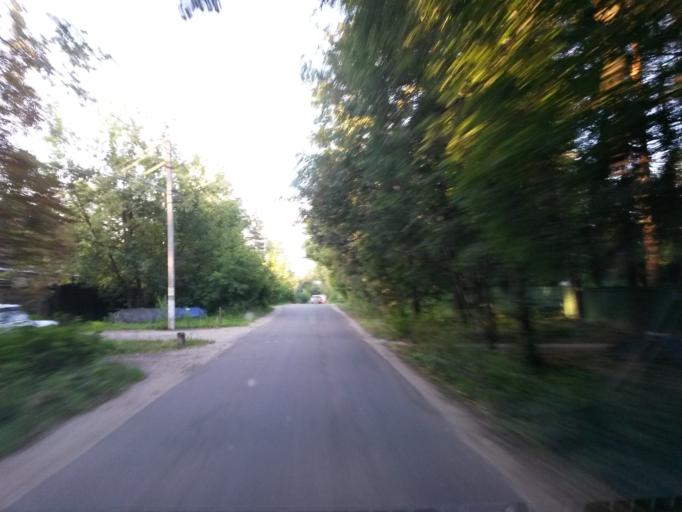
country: RU
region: Moskovskaya
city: Mamontovka
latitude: 55.9740
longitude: 37.8368
